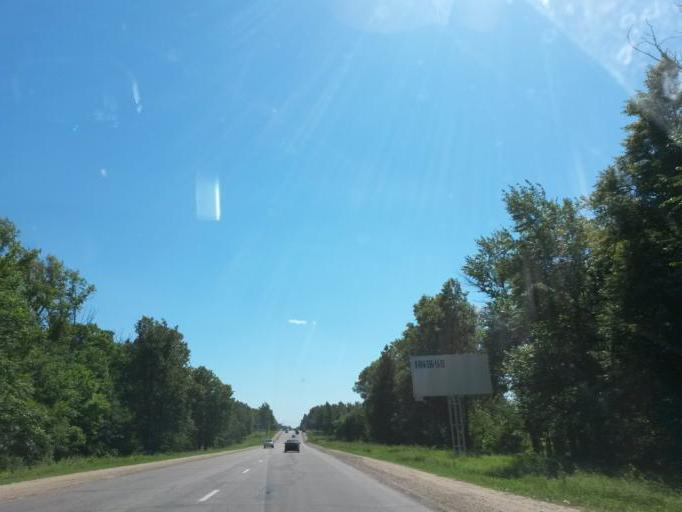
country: RU
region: Moskovskaya
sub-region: Chekhovskiy Rayon
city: Chekhov
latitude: 55.1243
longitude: 37.4502
